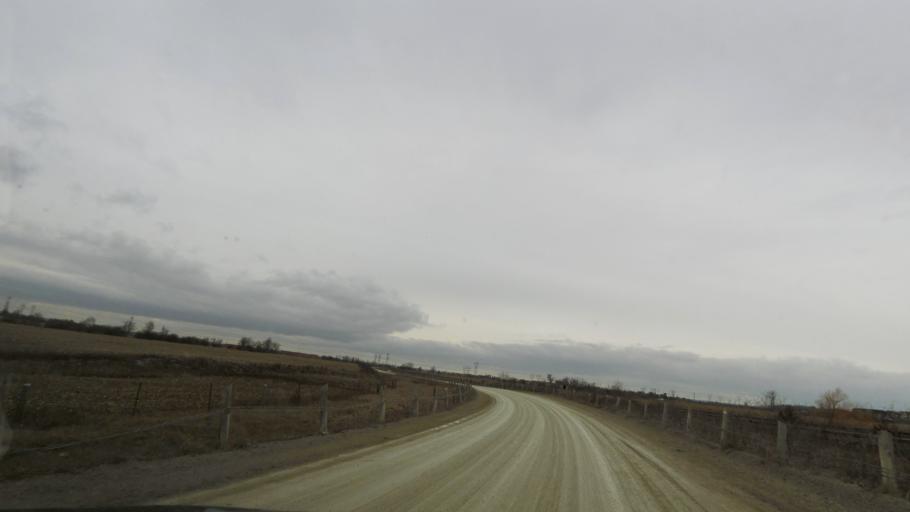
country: CA
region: Ontario
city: Vaughan
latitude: 43.8225
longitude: -79.6481
